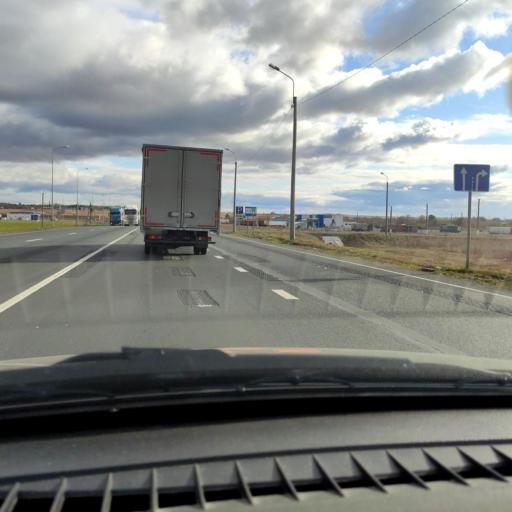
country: RU
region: Samara
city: Syzran'
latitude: 53.2107
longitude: 48.4777
